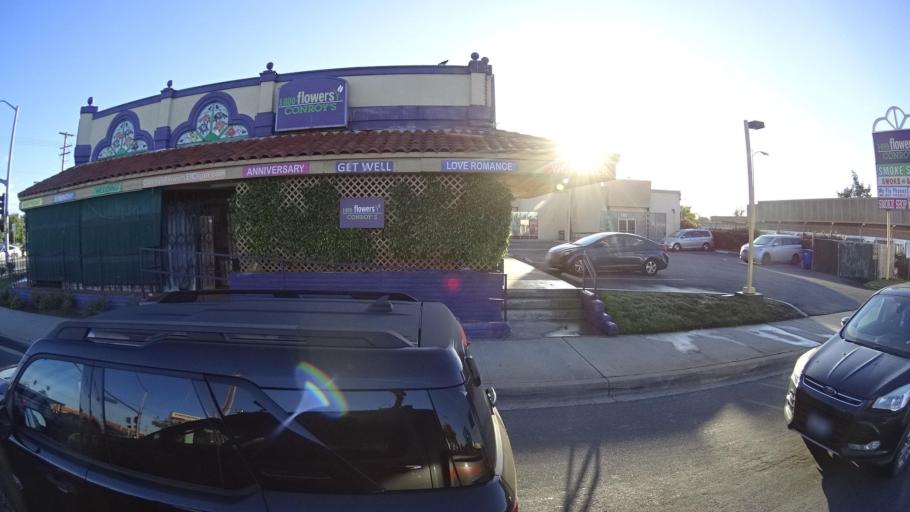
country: US
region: California
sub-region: San Diego County
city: Bostonia
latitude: 32.8074
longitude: -116.9356
